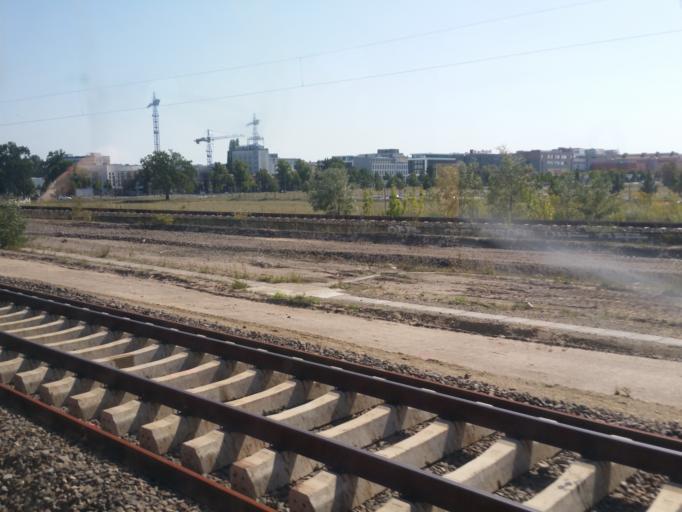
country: DE
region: Berlin
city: Adlershof
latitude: 52.4372
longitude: 13.5381
